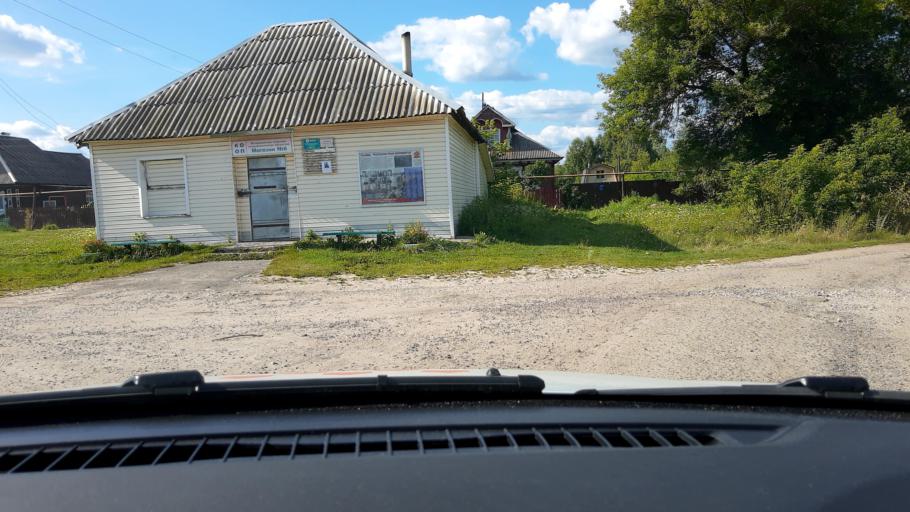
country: RU
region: Nizjnij Novgorod
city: Pamyat' Parizhskoy Kommuny
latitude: 56.2866
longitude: 44.4259
